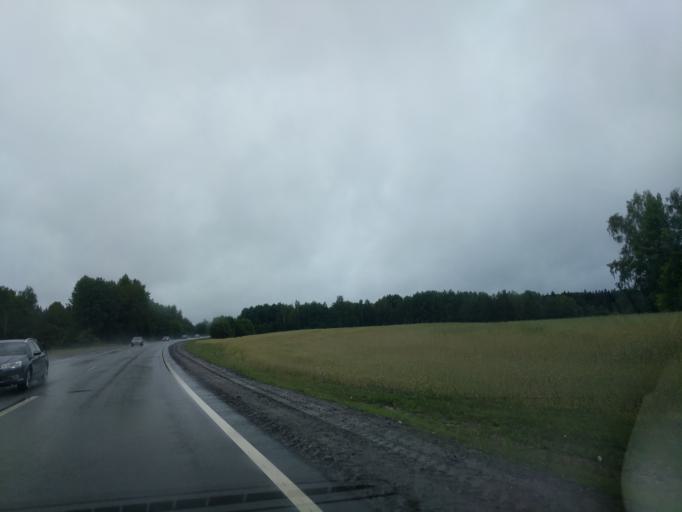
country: BY
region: Minsk
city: Syomkava
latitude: 54.1479
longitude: 27.5051
